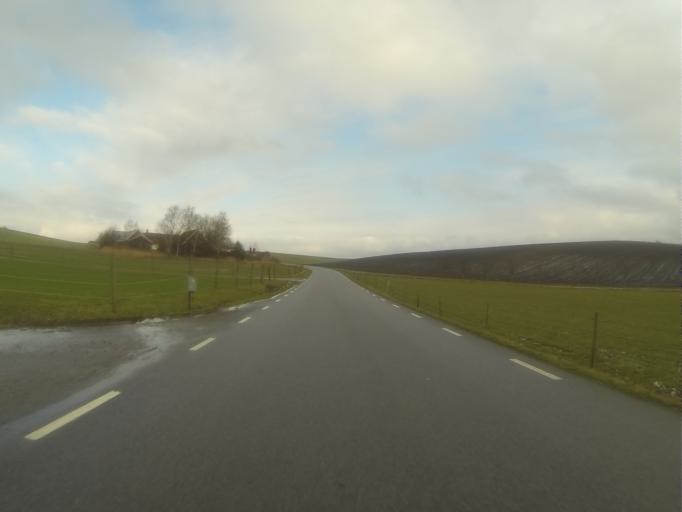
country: SE
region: Skane
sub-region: Svedala Kommun
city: Klagerup
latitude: 55.6098
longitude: 13.3046
